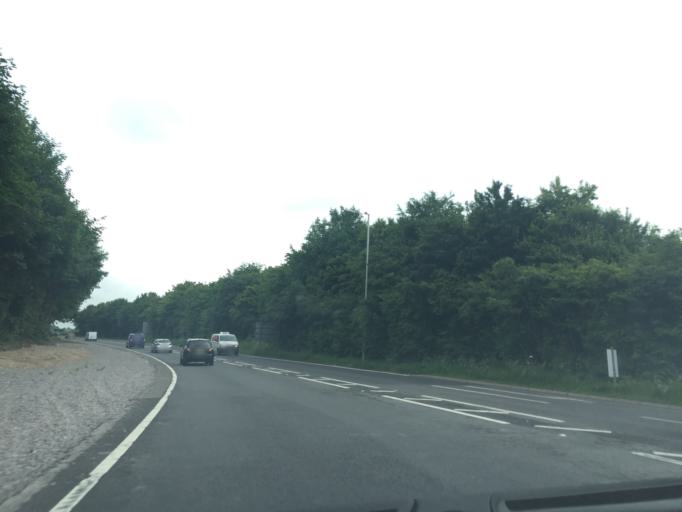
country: GB
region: England
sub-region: Dorset
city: Bovington Camp
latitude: 50.7574
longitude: -2.2115
